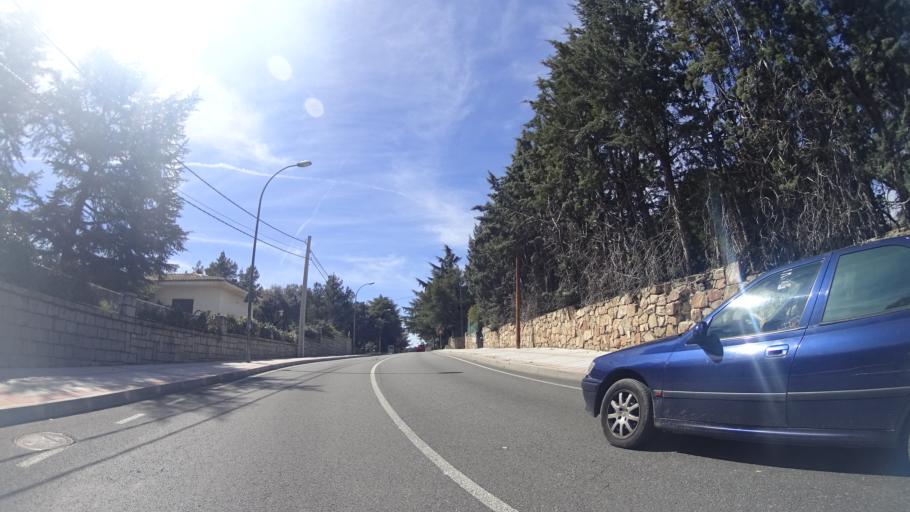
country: ES
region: Madrid
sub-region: Provincia de Madrid
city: Galapagar
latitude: 40.5916
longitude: -3.9867
